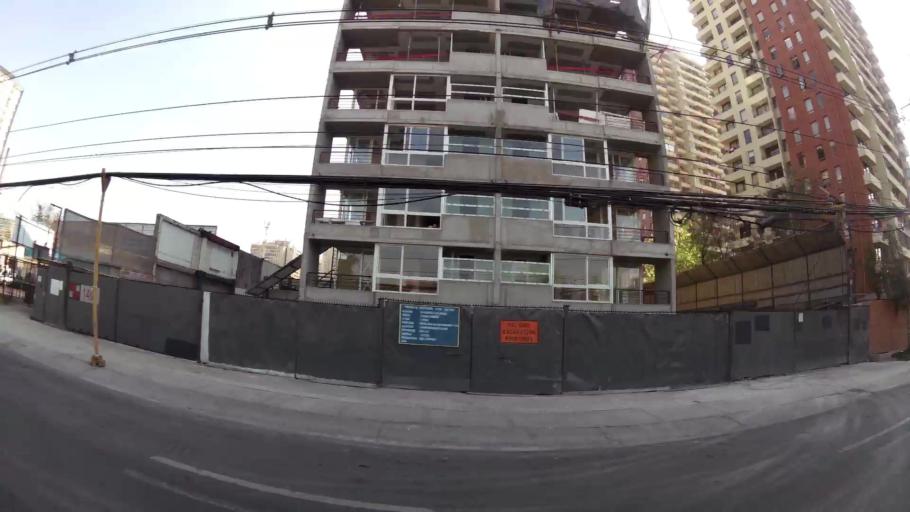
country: CL
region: Santiago Metropolitan
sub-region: Provincia de Santiago
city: Santiago
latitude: -33.4651
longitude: -70.6241
